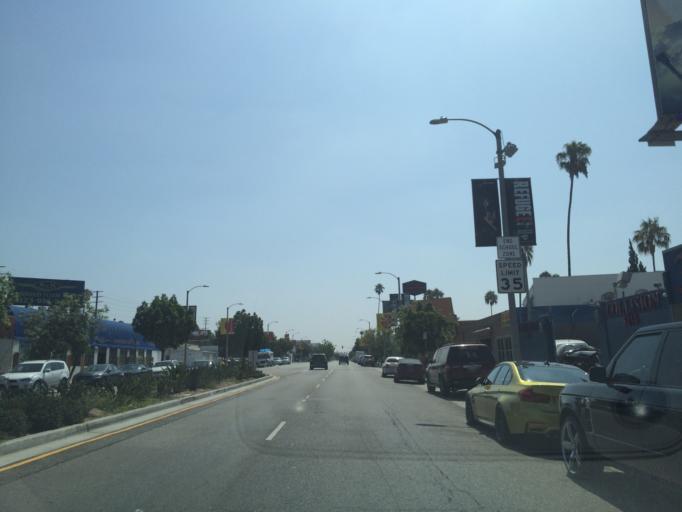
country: US
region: California
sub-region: Los Angeles County
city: West Hollywood
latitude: 34.0482
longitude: -118.3526
